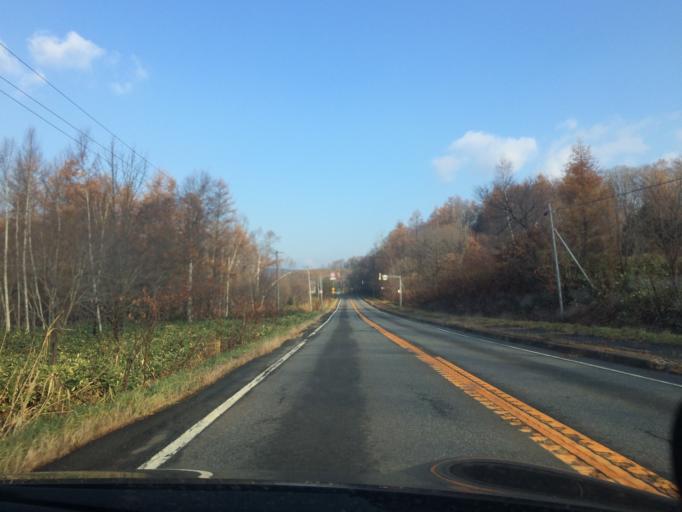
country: JP
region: Hokkaido
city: Shimo-furano
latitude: 42.8934
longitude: 142.4305
